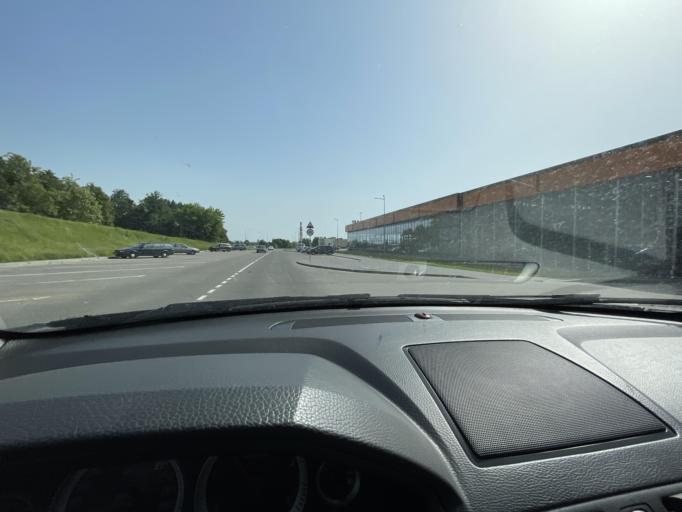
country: BY
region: Grodnenskaya
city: Hrodna
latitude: 53.6718
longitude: 23.8676
